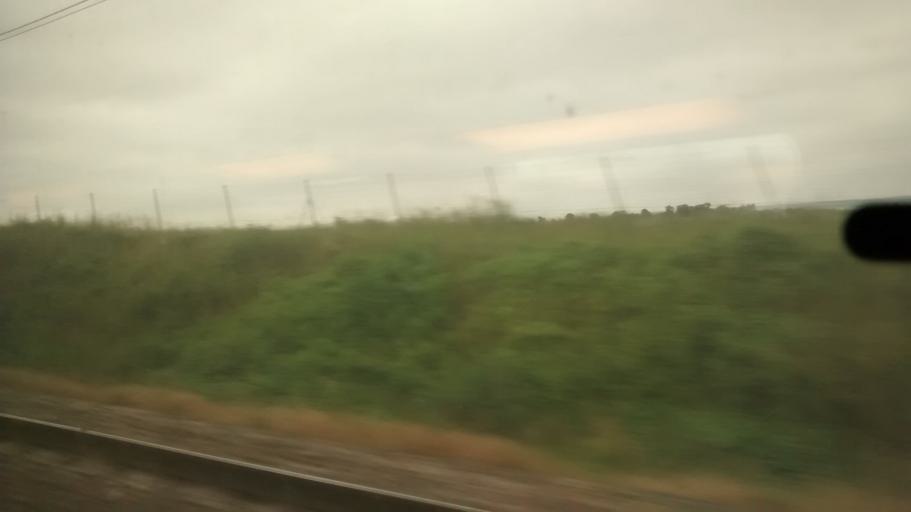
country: FR
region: Bourgogne
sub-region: Departement de l'Yonne
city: Villeneuve-la-Guyard
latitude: 48.3716
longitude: 3.0835
